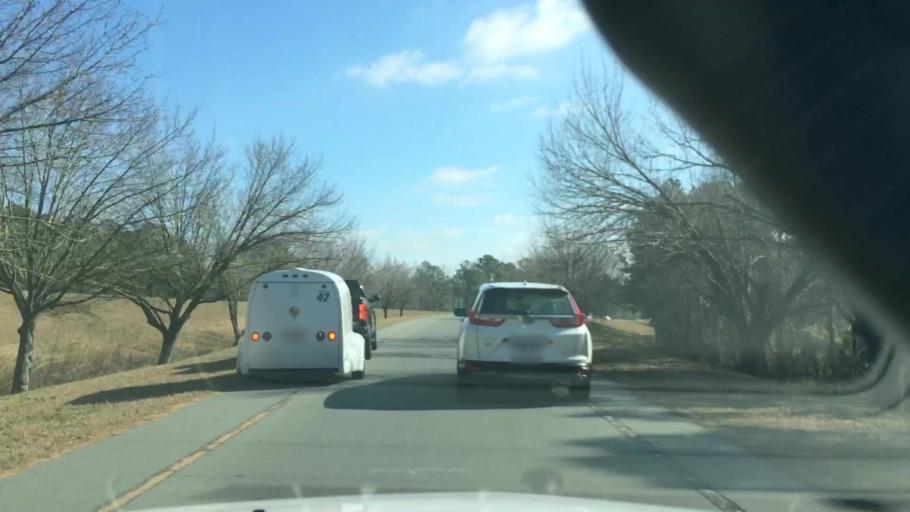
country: US
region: North Carolina
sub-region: Duplin County
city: Wallace
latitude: 34.7534
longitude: -77.9499
